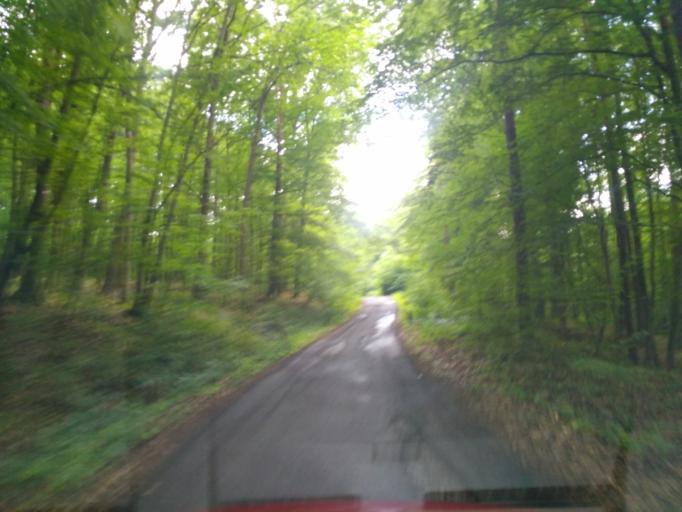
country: SK
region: Presovsky
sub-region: Okres Presov
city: Presov
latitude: 48.9664
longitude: 21.1703
